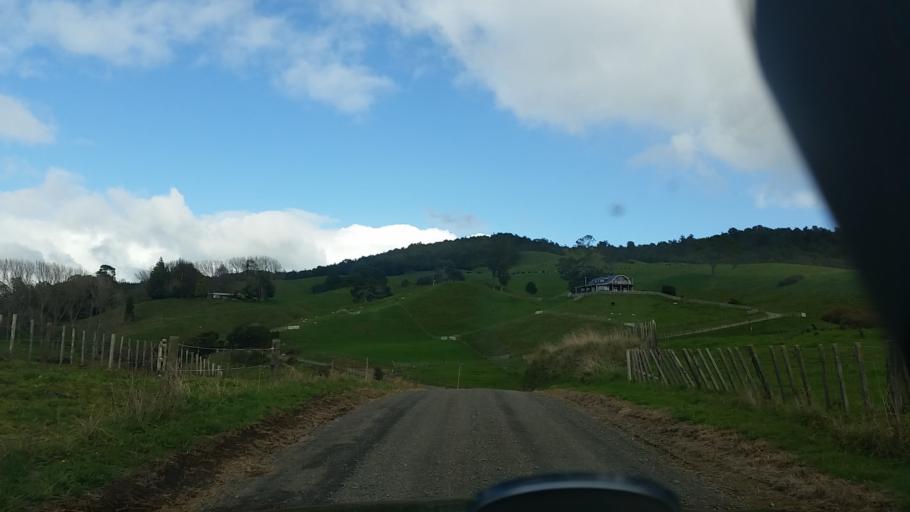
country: NZ
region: Waikato
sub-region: Matamata-Piako District
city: Matamata
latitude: -37.8222
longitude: 175.6758
